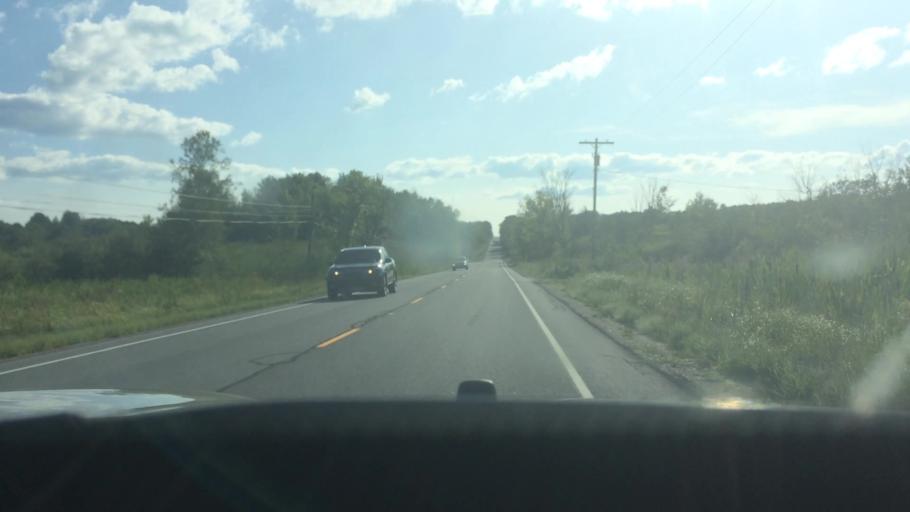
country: US
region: New York
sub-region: Franklin County
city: Malone
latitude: 44.7426
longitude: -74.5781
